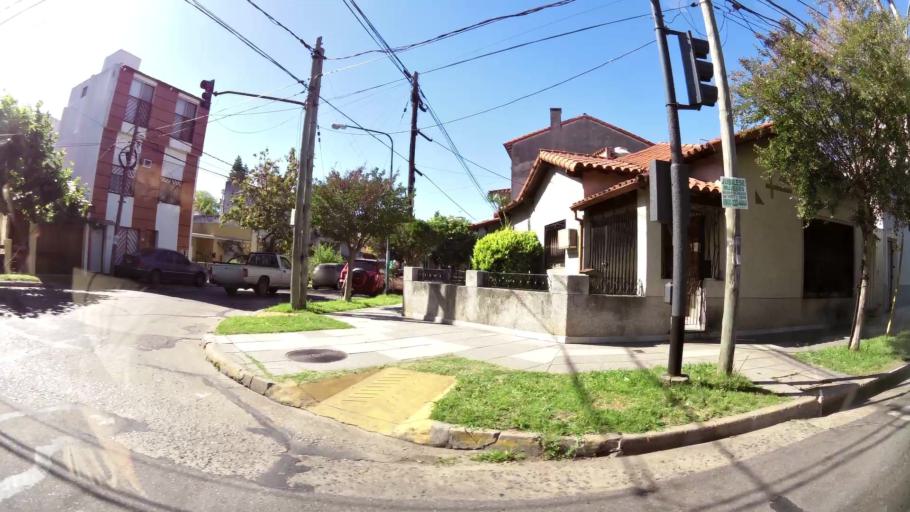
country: AR
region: Buenos Aires
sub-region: Partido de General San Martin
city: General San Martin
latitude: -34.5437
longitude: -58.5103
